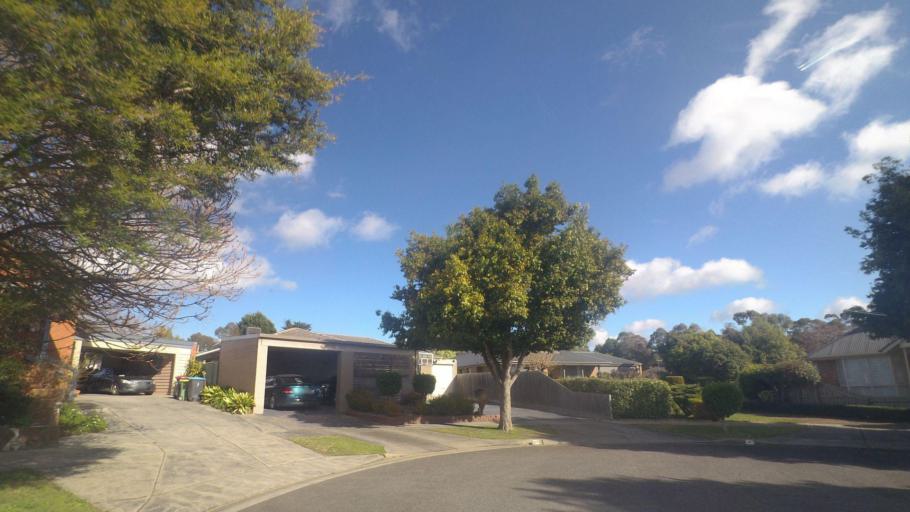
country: AU
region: Victoria
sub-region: Knox
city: Rowville
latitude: -37.9203
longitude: 145.2424
